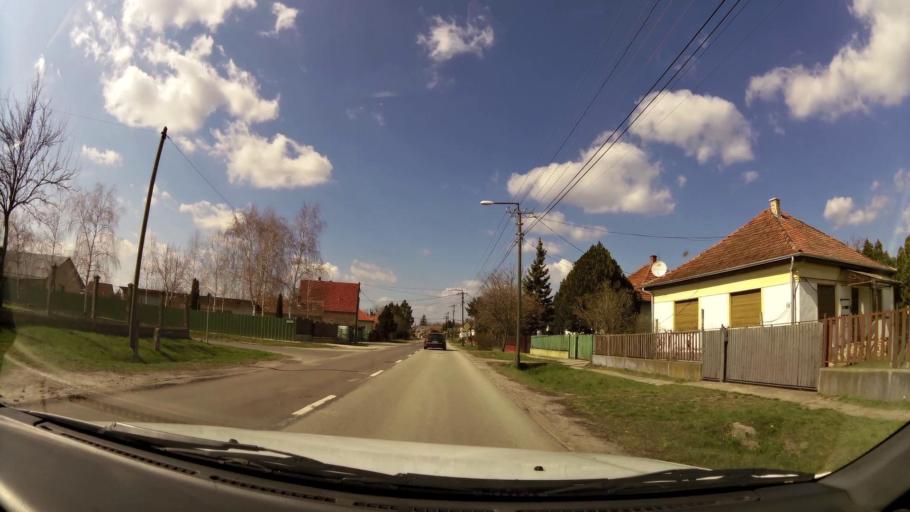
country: HU
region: Pest
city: Farmos
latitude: 47.3574
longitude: 19.8517
